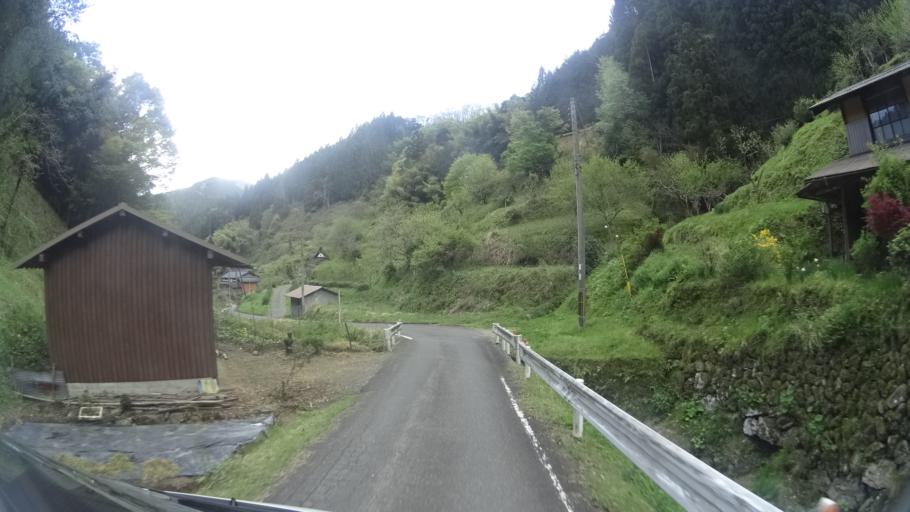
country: JP
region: Kyoto
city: Ayabe
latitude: 35.2567
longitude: 135.3354
